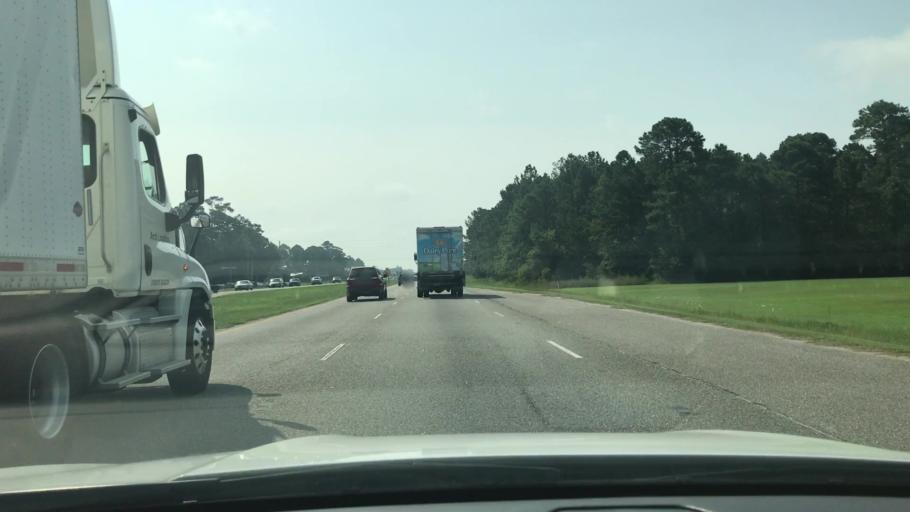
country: US
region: South Carolina
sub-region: Horry County
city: Red Hill
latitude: 33.8028
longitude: -79.0082
